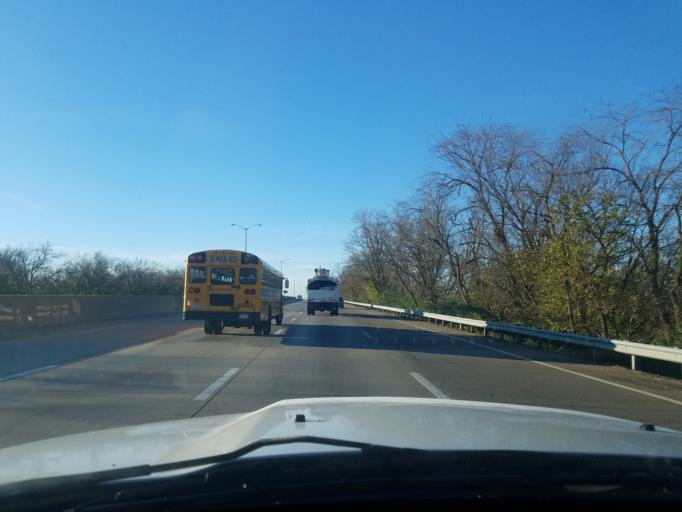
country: US
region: Kentucky
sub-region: Jefferson County
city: Shively
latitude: 38.2352
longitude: -85.8187
